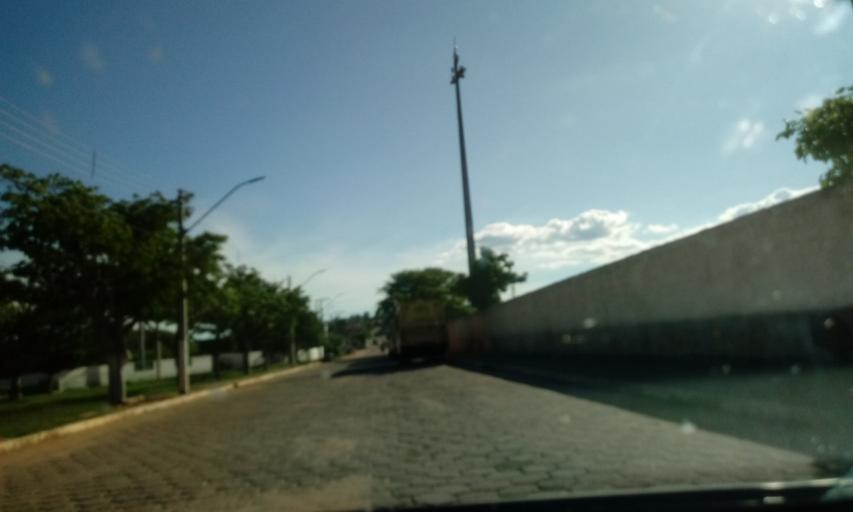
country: BR
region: Bahia
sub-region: Riacho De Santana
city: Riacho de Santana
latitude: -13.7741
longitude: -42.7176
